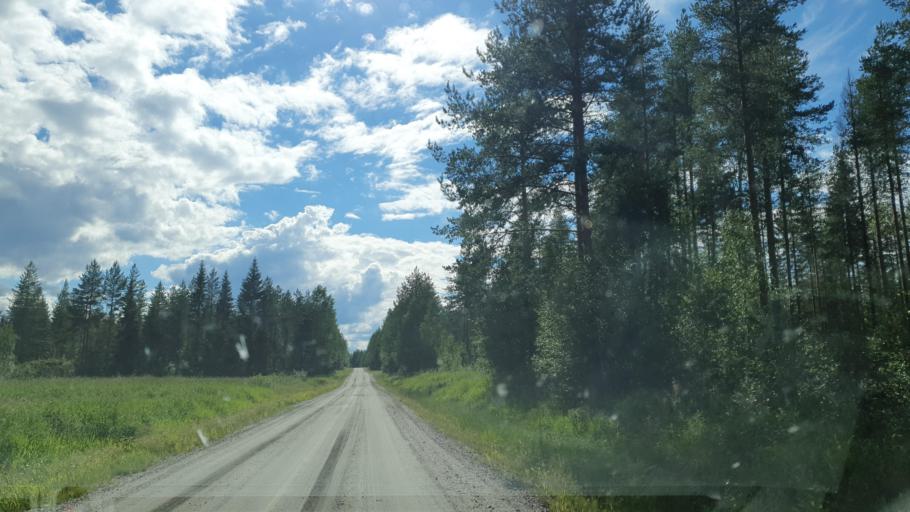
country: FI
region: Kainuu
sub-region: Kehys-Kainuu
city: Kuhmo
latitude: 64.1464
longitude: 29.7138
